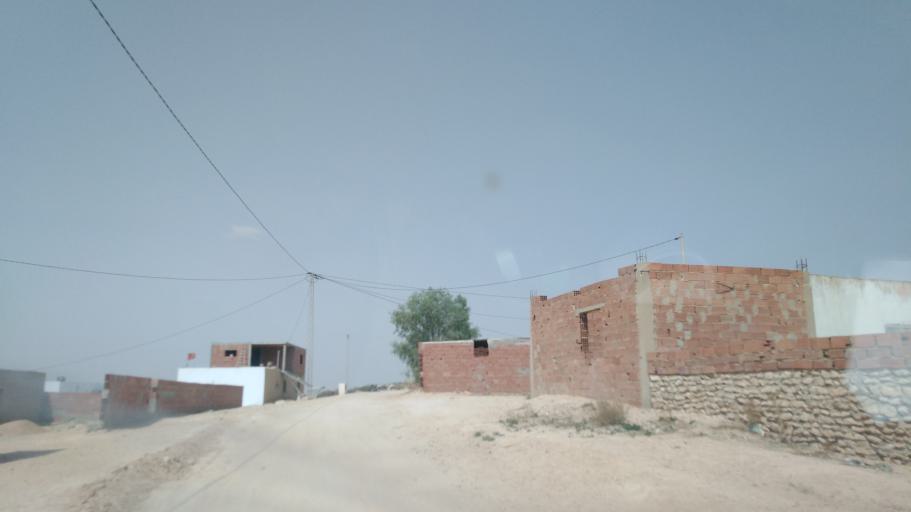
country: TN
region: Safaqis
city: Sfax
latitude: 34.6416
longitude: 10.5616
